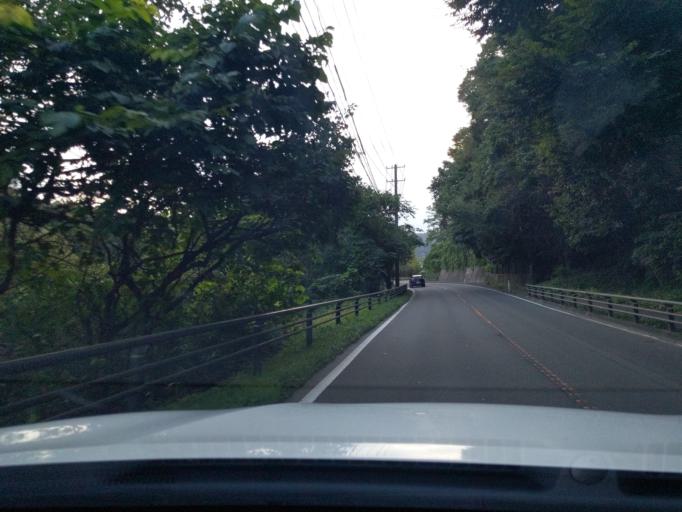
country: JP
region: Miyagi
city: Sendai
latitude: 38.2654
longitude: 140.8244
